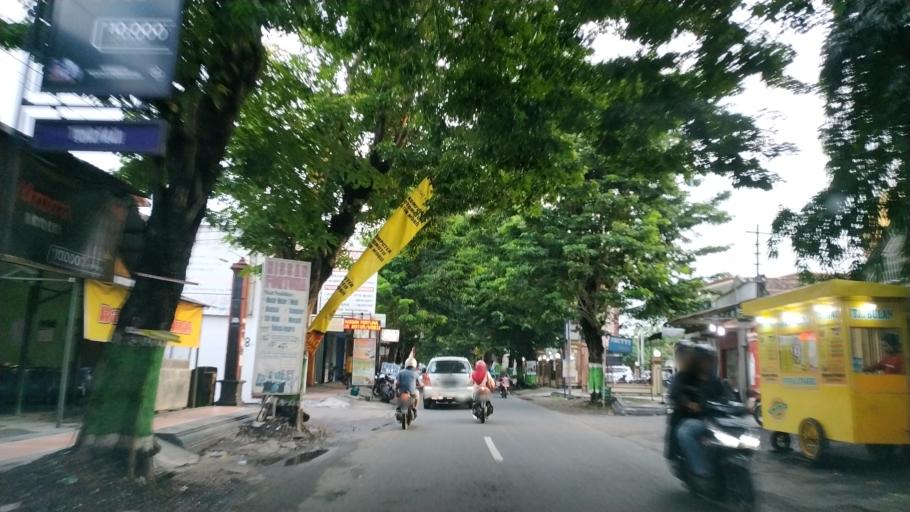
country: ID
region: Central Java
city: Kudus
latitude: -6.8092
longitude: 110.8550
